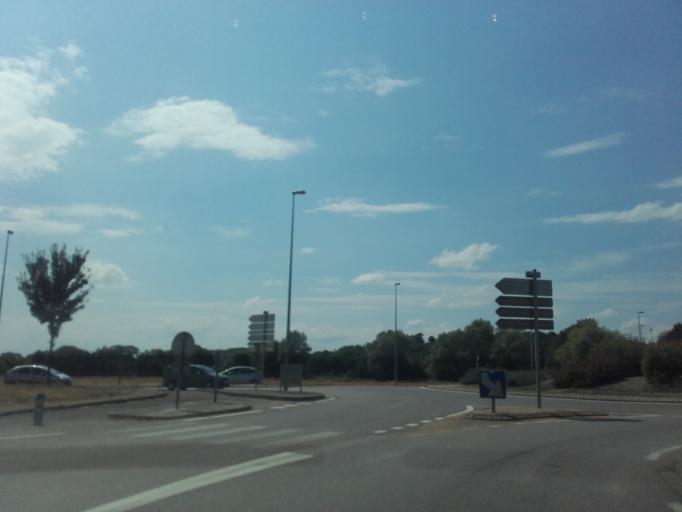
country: FR
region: Rhone-Alpes
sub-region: Departement de l'Ain
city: Meximieux
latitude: 45.8973
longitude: 5.1924
